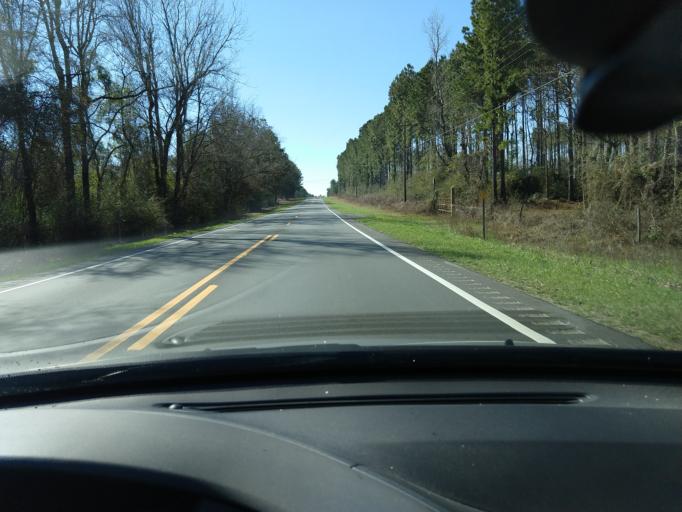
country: US
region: Alabama
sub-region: Covington County
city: Andalusia
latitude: 31.2220
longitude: -86.5316
